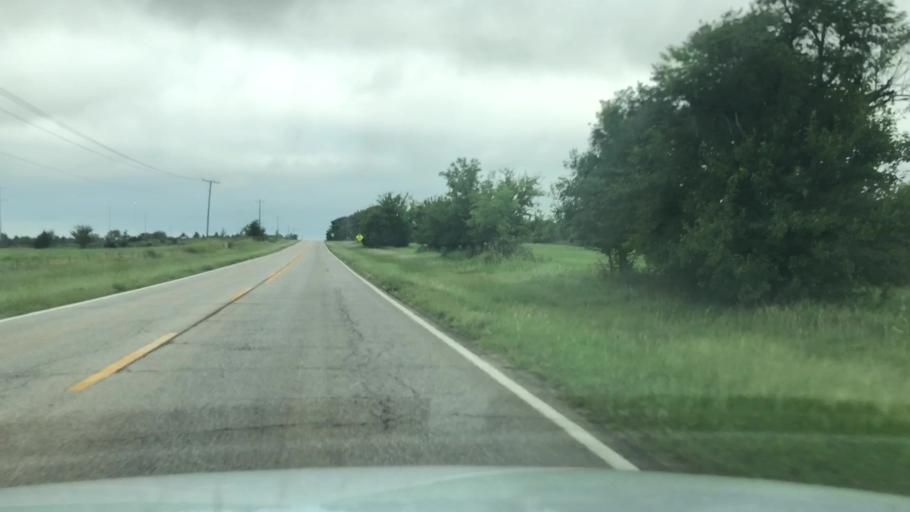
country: US
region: Oklahoma
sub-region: Nowata County
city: Nowata
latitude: 36.7073
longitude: -95.6547
